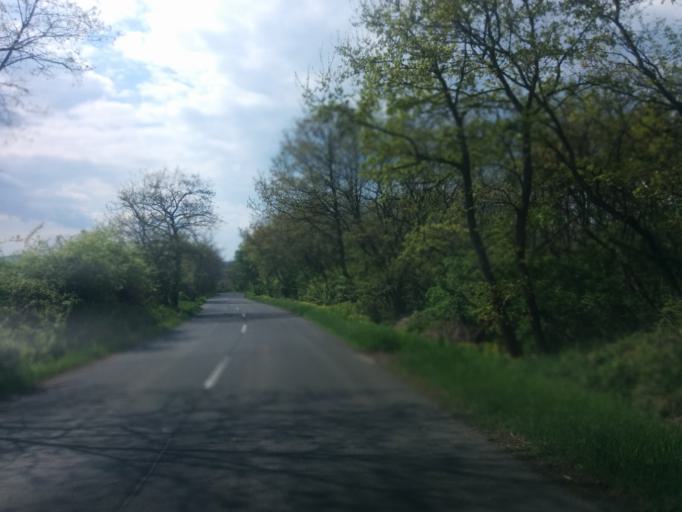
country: HU
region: Pest
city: Acsa
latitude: 47.8443
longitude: 19.3220
